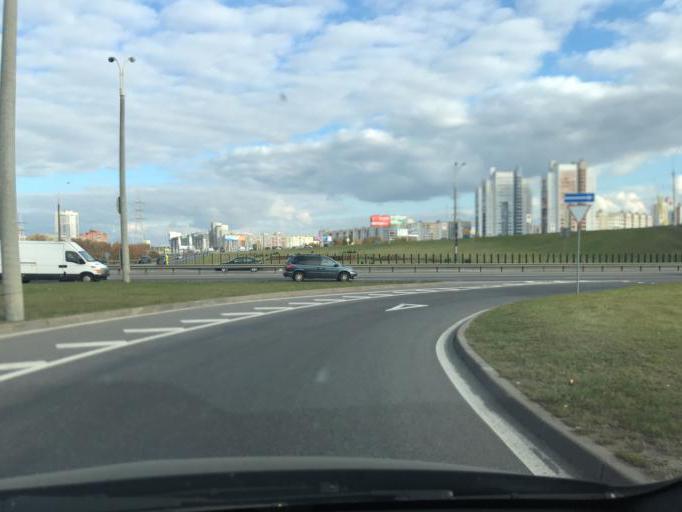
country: BY
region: Minsk
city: Borovlyany
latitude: 53.9415
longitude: 27.6720
